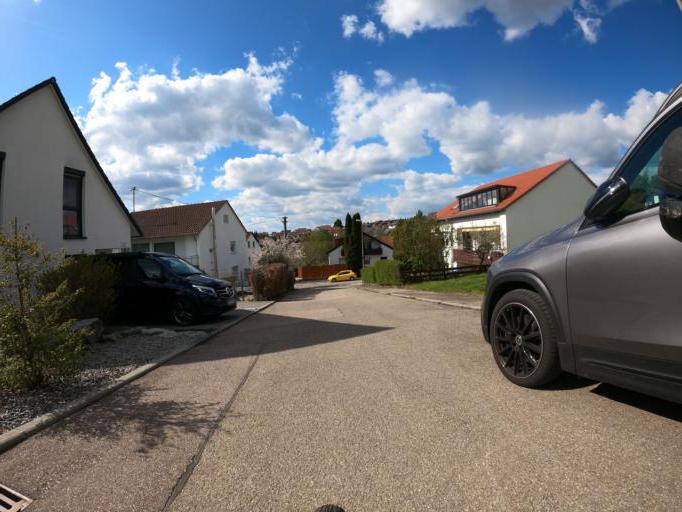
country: DE
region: Baden-Wuerttemberg
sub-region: Regierungsbezirk Stuttgart
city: Weil der Stadt
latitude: 48.7223
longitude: 8.8990
